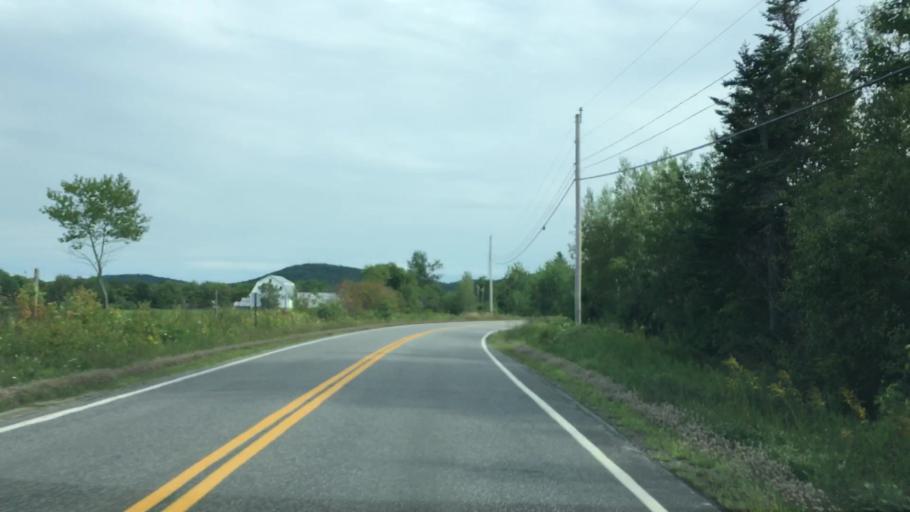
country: US
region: Maine
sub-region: Waldo County
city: Belfast
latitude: 44.3766
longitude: -69.0322
